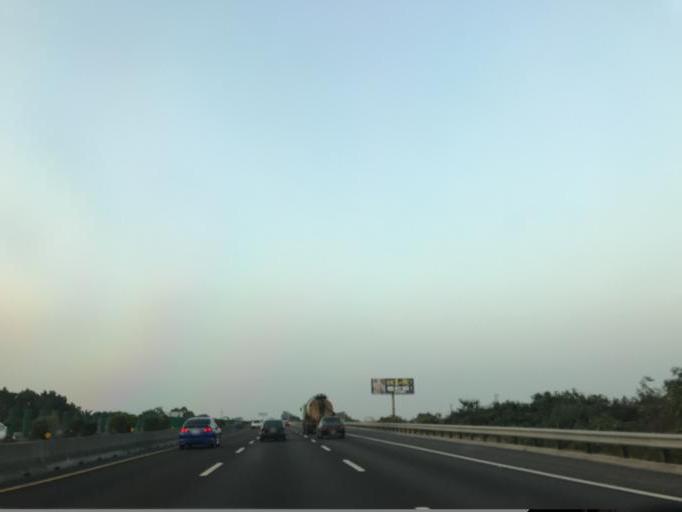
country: TW
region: Taiwan
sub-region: Yunlin
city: Douliu
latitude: 23.7187
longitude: 120.4758
